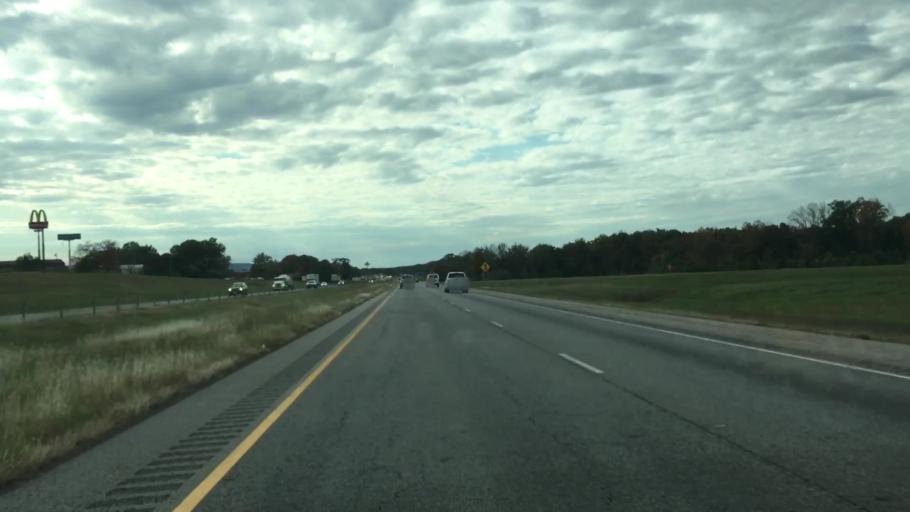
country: US
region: Arkansas
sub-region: Conway County
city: Morrilton
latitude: 35.1743
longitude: -92.7189
